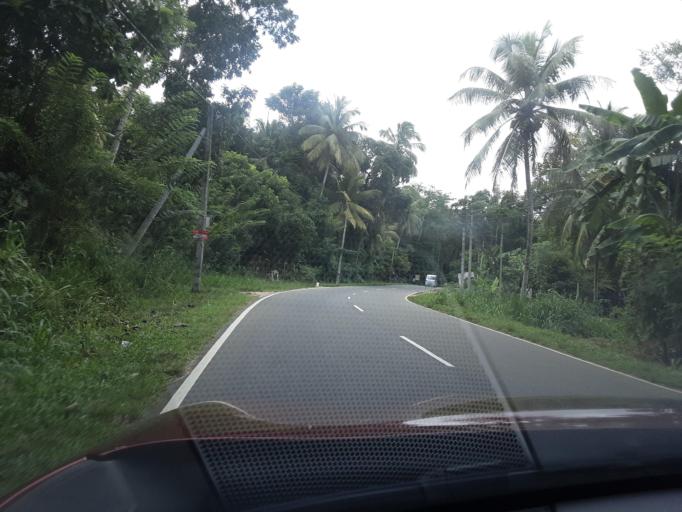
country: LK
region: Uva
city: Monaragala
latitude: 6.8952
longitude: 81.2898
